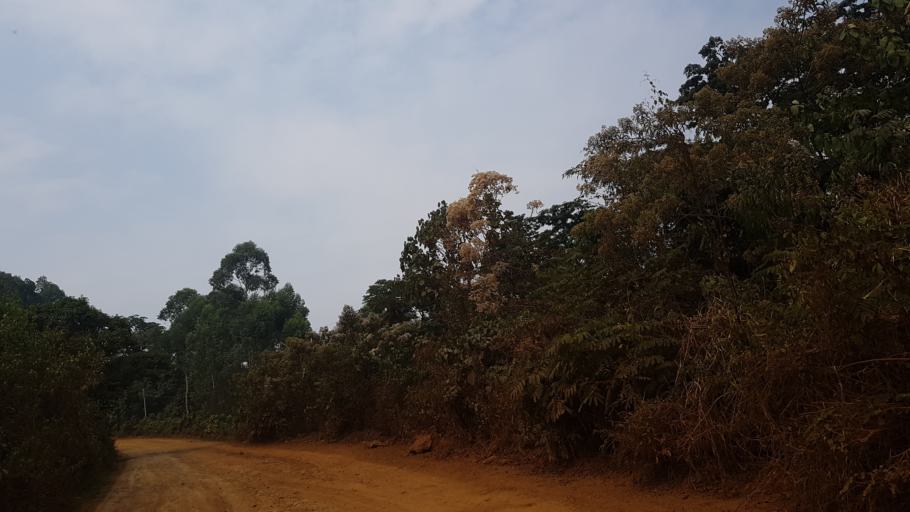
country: ET
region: Oromiya
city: Gore
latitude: 7.8229
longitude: 35.4592
